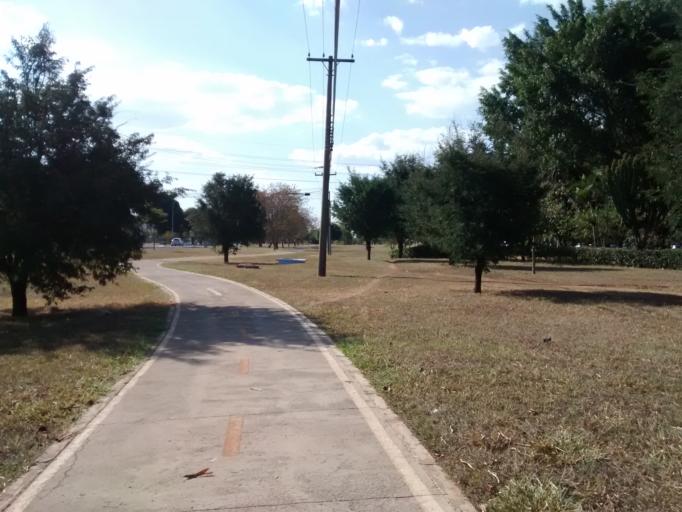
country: BR
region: Federal District
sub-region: Brasilia
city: Brasilia
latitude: -15.7985
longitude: -47.9331
